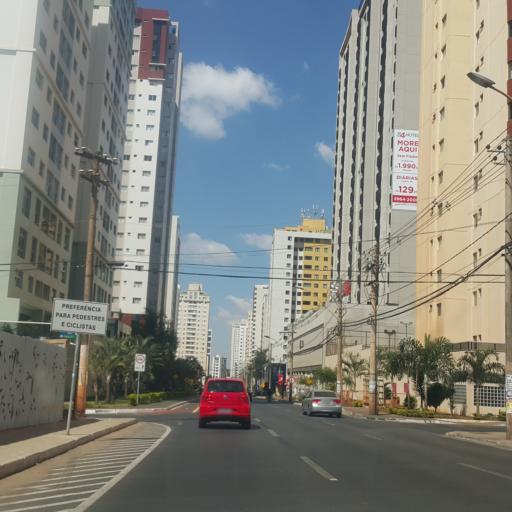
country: BR
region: Federal District
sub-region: Brasilia
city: Brasilia
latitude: -15.8361
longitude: -48.0401
